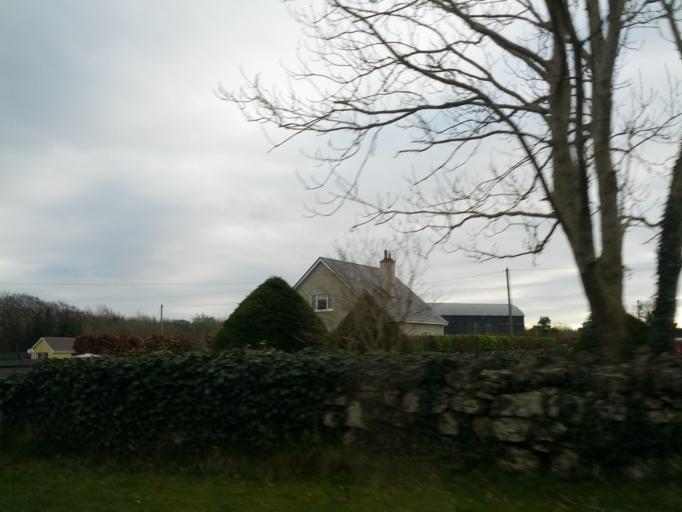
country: IE
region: Connaught
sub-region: County Galway
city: Oranmore
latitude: 53.1798
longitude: -8.9028
